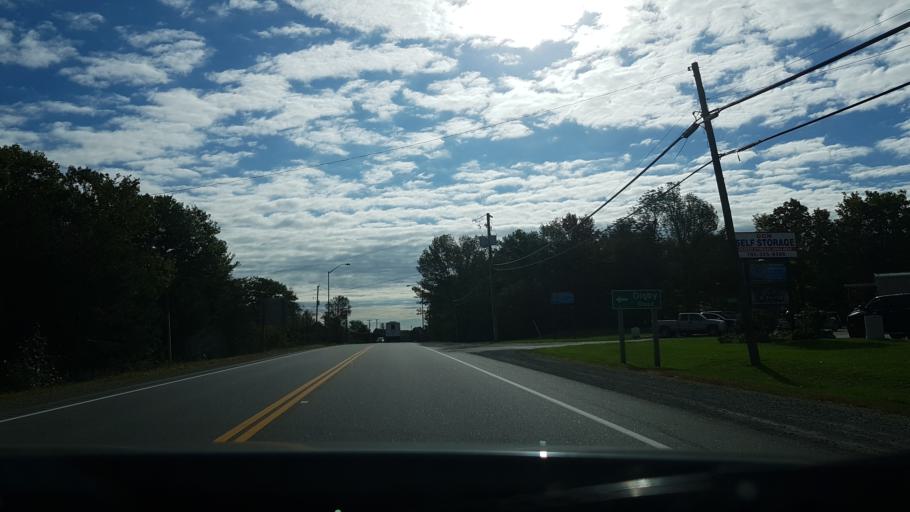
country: CA
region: Ontario
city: Orillia
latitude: 44.6179
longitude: -79.5061
